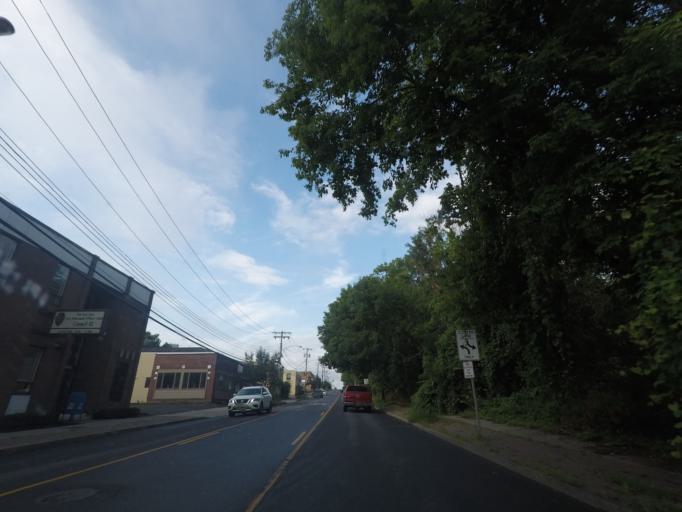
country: US
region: New York
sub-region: Albany County
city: West Albany
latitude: 42.6797
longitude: -73.7945
